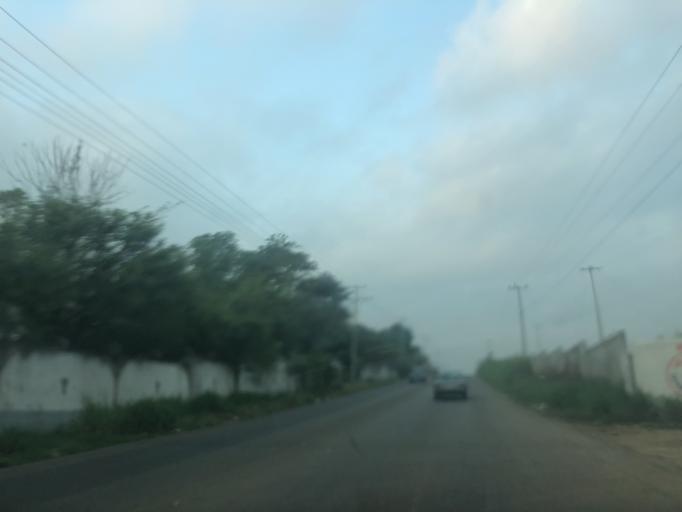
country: MX
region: Chiapas
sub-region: Reforma
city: El Carmen (El Limon)
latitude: 17.8621
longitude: -93.1571
